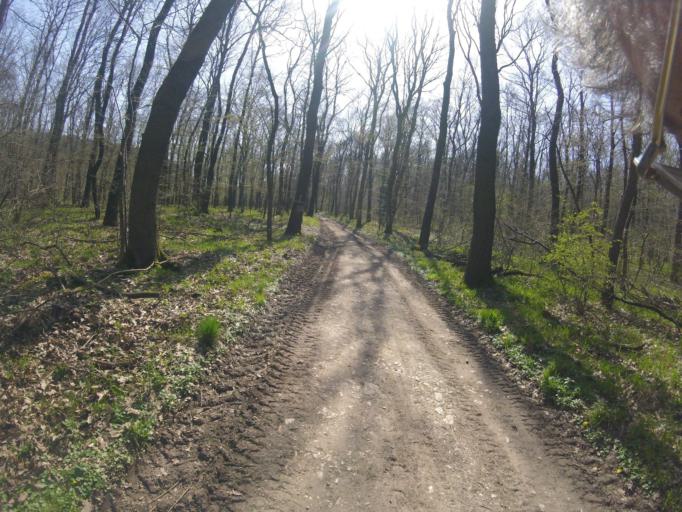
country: HU
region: Pest
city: Pilisszanto
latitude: 47.6522
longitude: 18.8651
